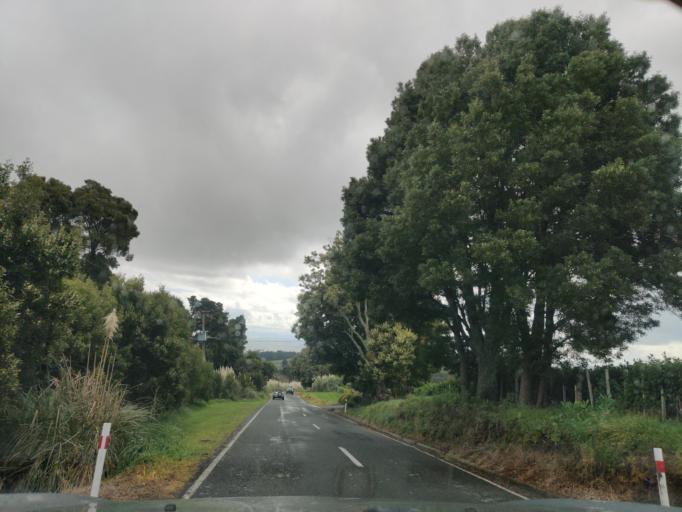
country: NZ
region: Hawke's Bay
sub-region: Hastings District
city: Hastings
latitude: -39.6921
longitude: 176.9004
